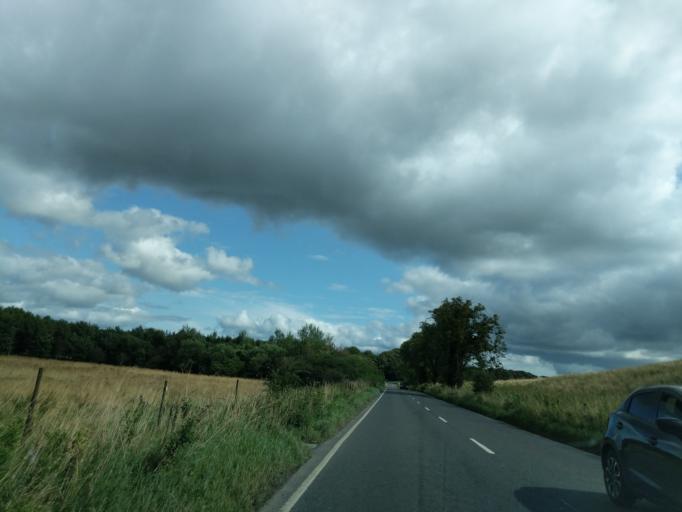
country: GB
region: Scotland
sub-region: Fife
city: Dunfermline
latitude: 56.1063
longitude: -3.4603
